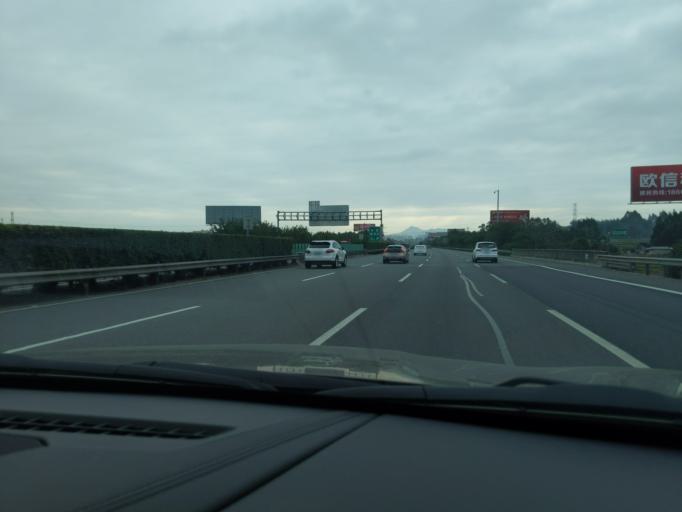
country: CN
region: Fujian
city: Neikeng
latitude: 24.7709
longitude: 118.4533
